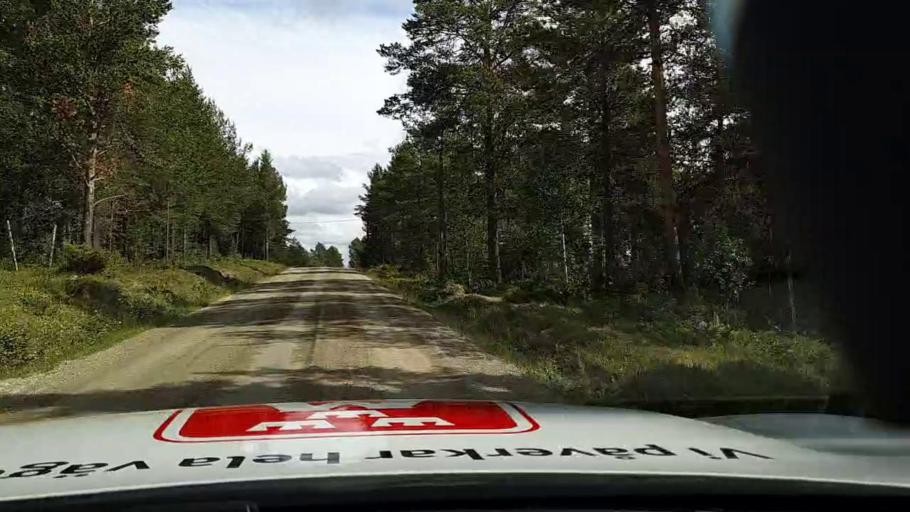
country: SE
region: Jaemtland
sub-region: Are Kommun
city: Jarpen
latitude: 62.5506
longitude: 13.4488
